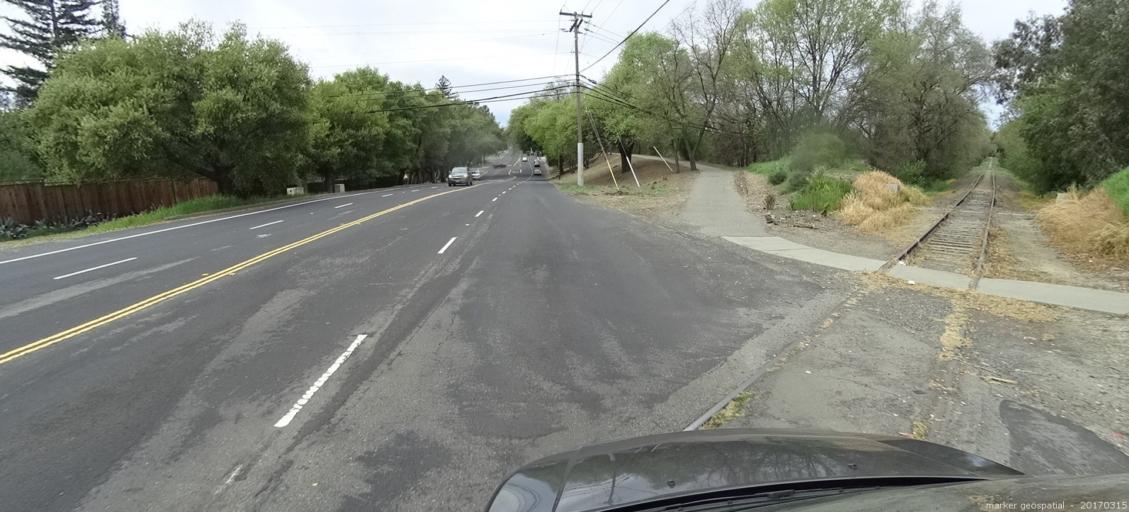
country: US
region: California
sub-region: Sacramento County
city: Sacramento
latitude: 38.5388
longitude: -121.5057
